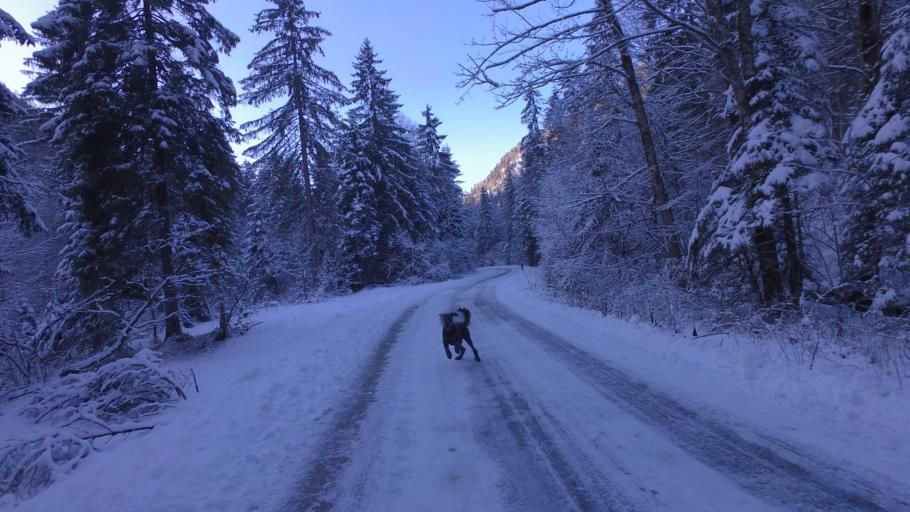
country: DE
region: Bavaria
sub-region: Upper Bavaria
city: Ruhpolding
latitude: 47.7277
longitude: 12.5796
